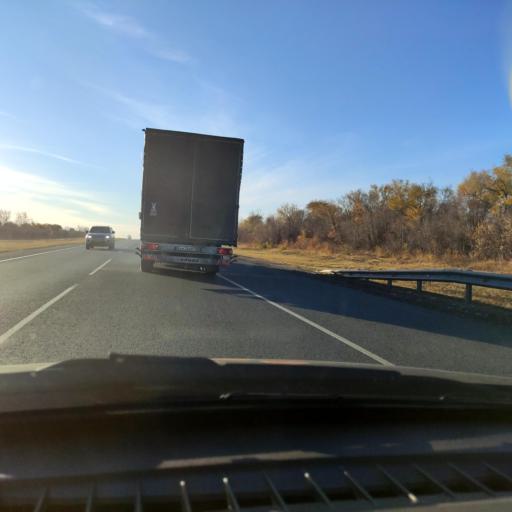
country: RU
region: Samara
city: Varlamovo
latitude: 53.1943
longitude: 48.2507
